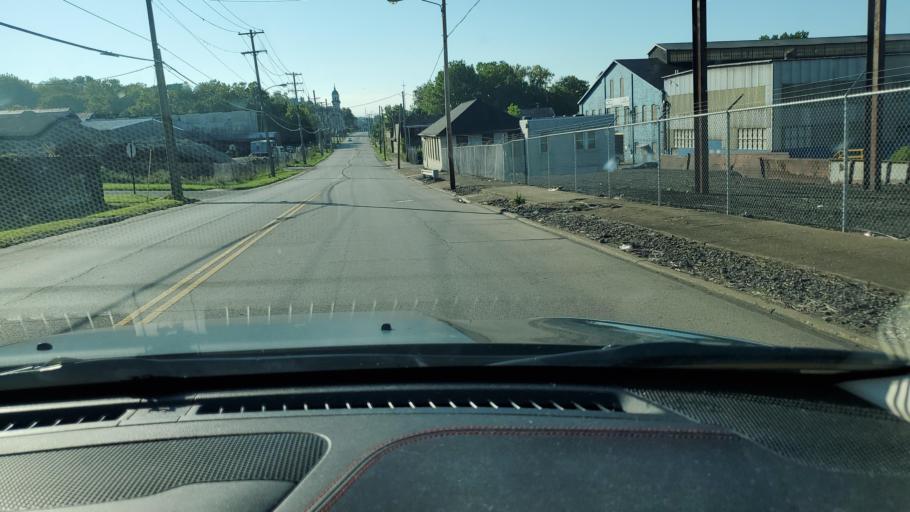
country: US
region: Ohio
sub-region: Mahoning County
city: Campbell
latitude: 41.0859
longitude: -80.6217
